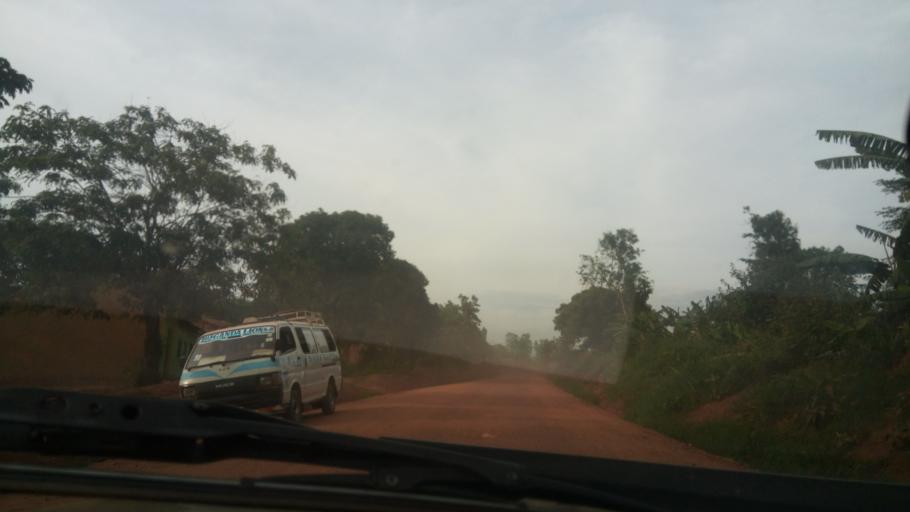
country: UG
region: Central Region
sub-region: Mityana District
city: Mityana
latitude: 0.5572
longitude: 32.1936
